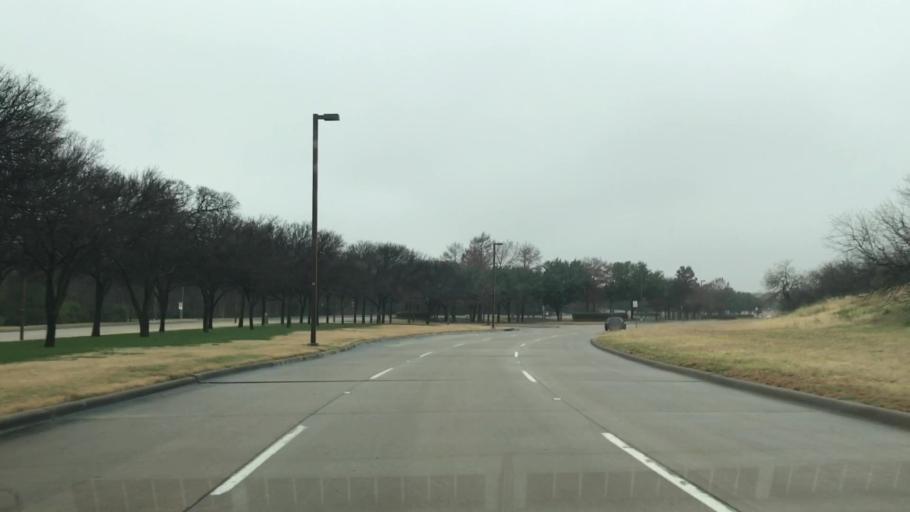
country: US
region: Texas
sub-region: Dallas County
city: Farmers Branch
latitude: 32.8900
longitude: -96.9462
